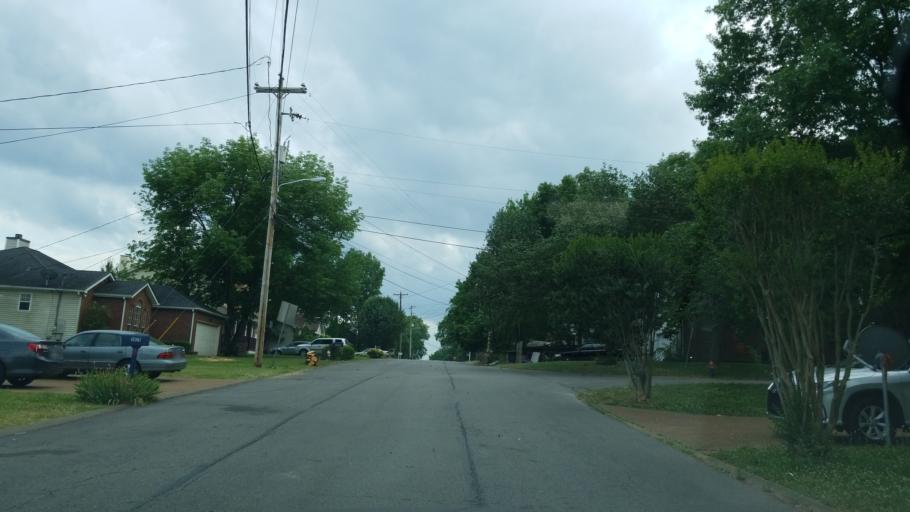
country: US
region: Tennessee
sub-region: Rutherford County
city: La Vergne
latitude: 36.0777
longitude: -86.6145
